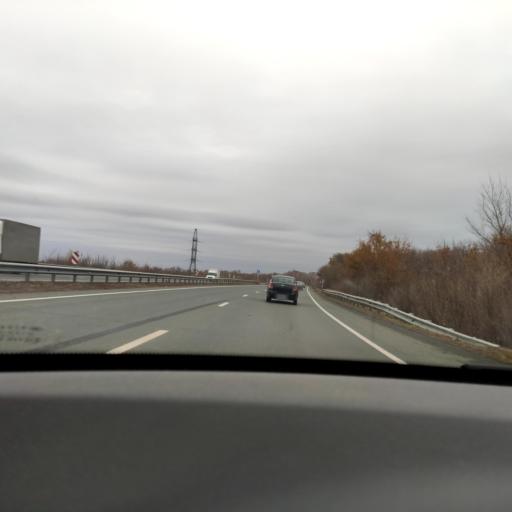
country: RU
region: Samara
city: Novokuybyshevsk
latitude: 53.0241
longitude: 49.9859
